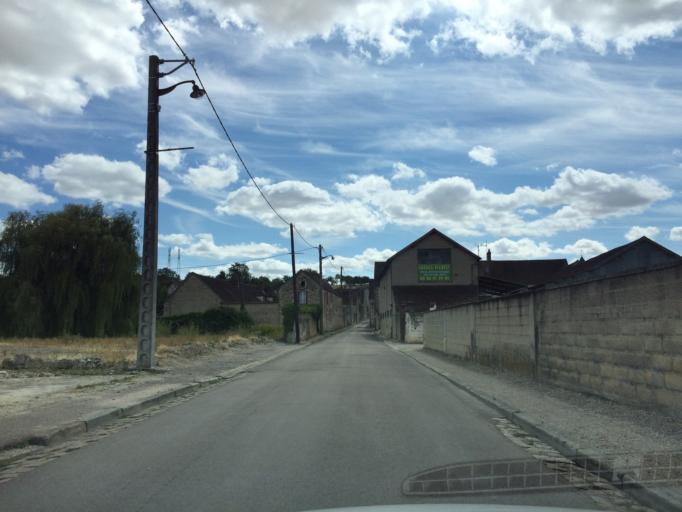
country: FR
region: Bourgogne
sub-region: Departement de l'Yonne
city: Laroche-Saint-Cydroine
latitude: 47.9475
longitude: 3.4740
